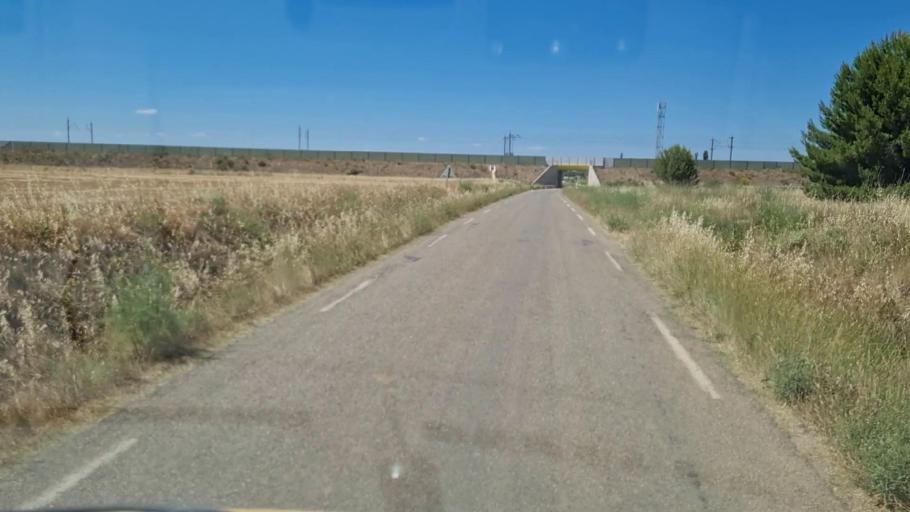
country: FR
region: Languedoc-Roussillon
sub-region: Departement du Gard
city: Codognan
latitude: 43.7112
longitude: 4.2287
